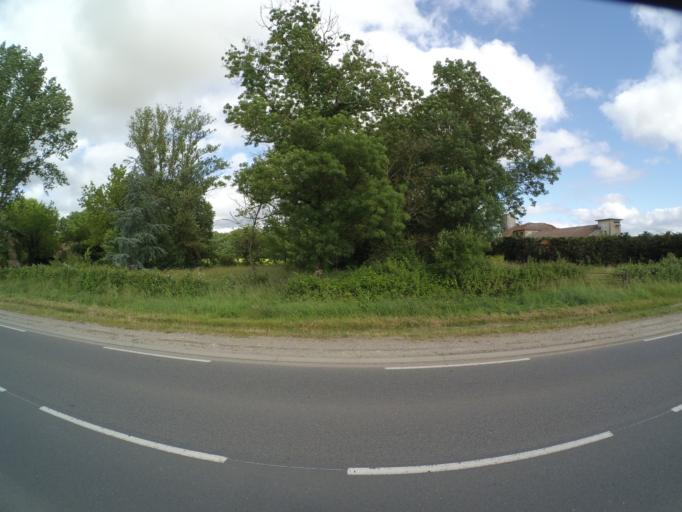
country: FR
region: Aquitaine
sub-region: Departement de la Gironde
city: Saint-Louis-de-Montferrand
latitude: 44.9316
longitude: -0.5619
